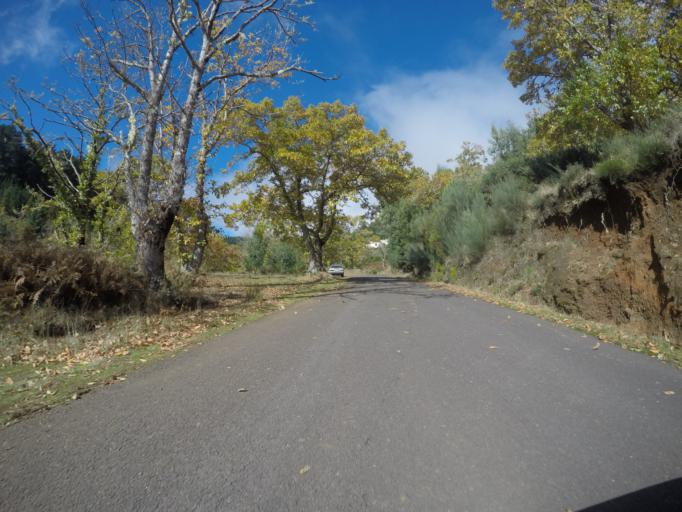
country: PT
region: Madeira
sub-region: Funchal
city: Nossa Senhora do Monte
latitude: 32.7012
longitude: -16.8860
